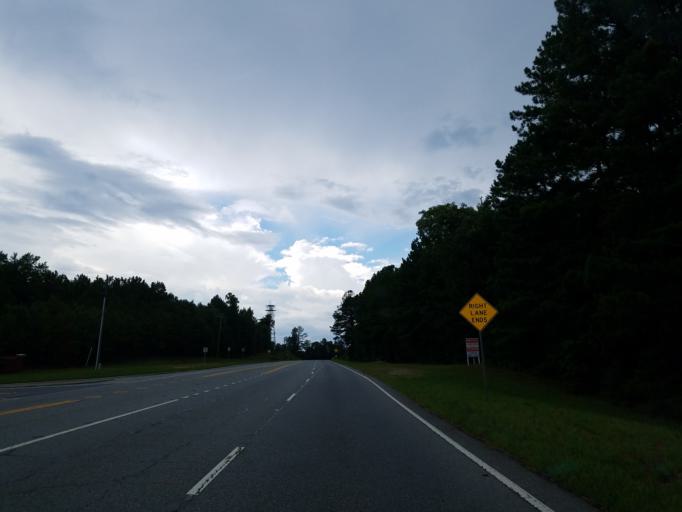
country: US
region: Georgia
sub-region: Bartow County
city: Adairsville
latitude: 34.3149
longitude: -84.8945
